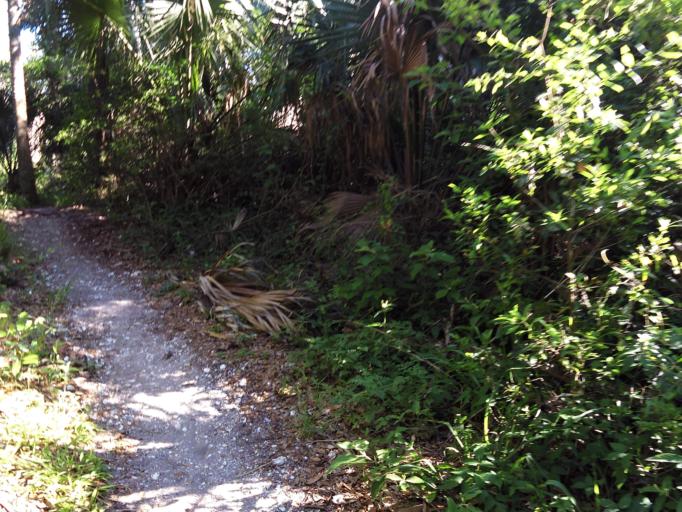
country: US
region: Florida
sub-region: Duval County
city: Atlantic Beach
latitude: 30.3822
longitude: -81.4841
